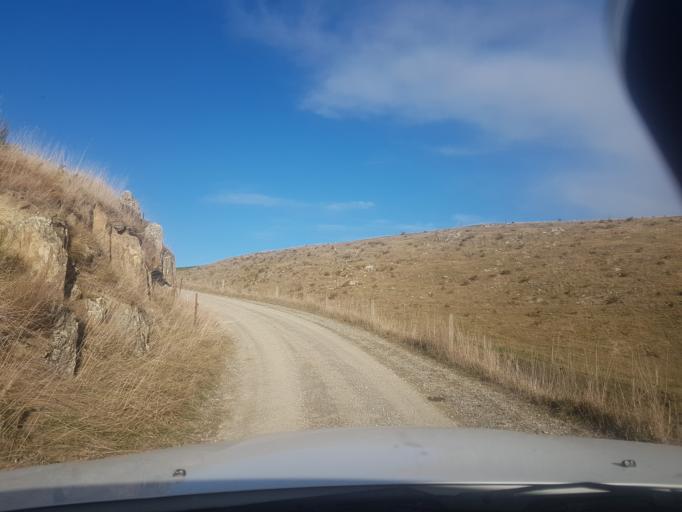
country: NZ
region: Canterbury
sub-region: Timaru District
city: Pleasant Point
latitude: -44.1760
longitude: 170.8882
